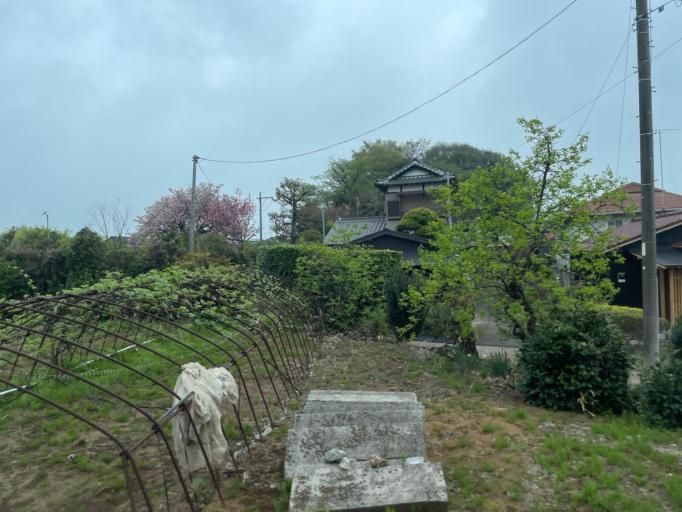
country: JP
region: Saitama
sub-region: Kawaguchi-shi
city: Hatogaya-honcho
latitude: 35.8607
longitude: 139.7217
